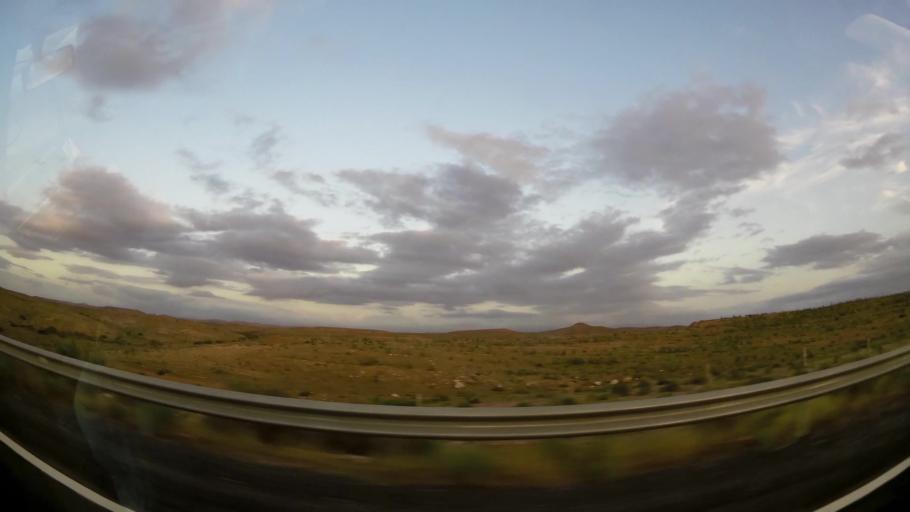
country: MA
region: Oriental
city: Taourirt
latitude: 34.5638
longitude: -2.8340
